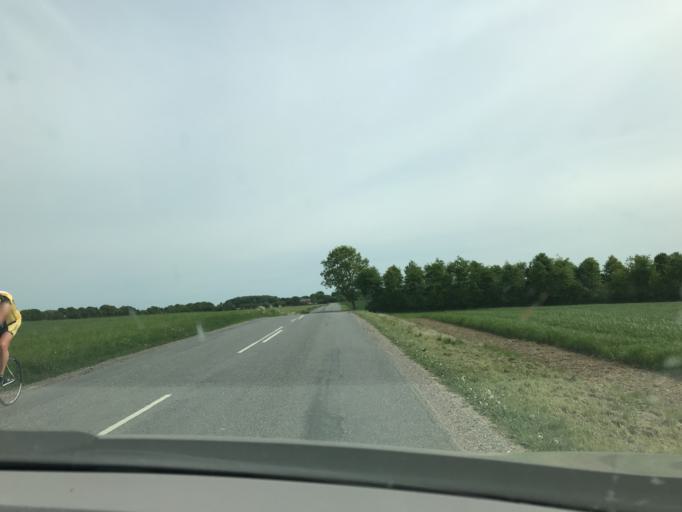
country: DK
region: Central Jutland
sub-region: Norddjurs Kommune
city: Allingabro
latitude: 56.5354
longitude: 10.3056
